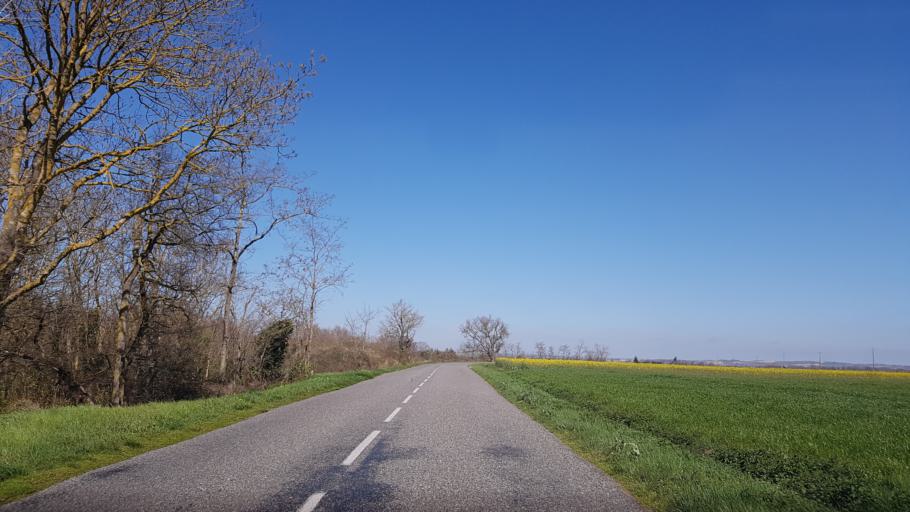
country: FR
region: Languedoc-Roussillon
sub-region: Departement de l'Aude
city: Belpech
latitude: 43.1503
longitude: 1.7050
